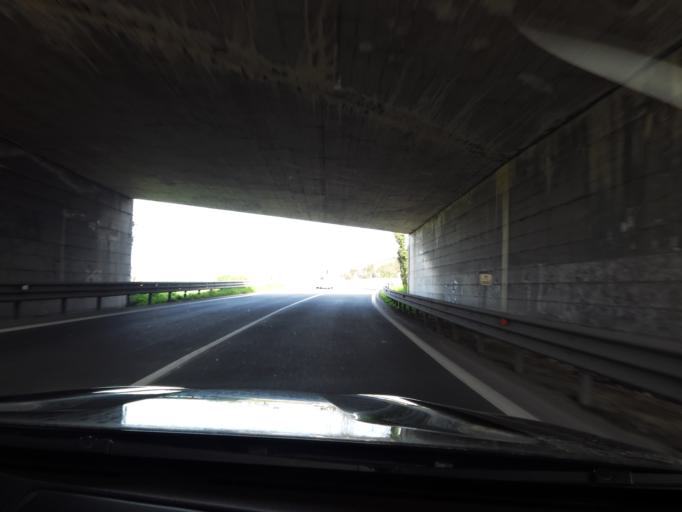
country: IT
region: The Marches
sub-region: Provincia di Ancona
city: Loreto Stazione
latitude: 43.4450
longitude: 13.6302
